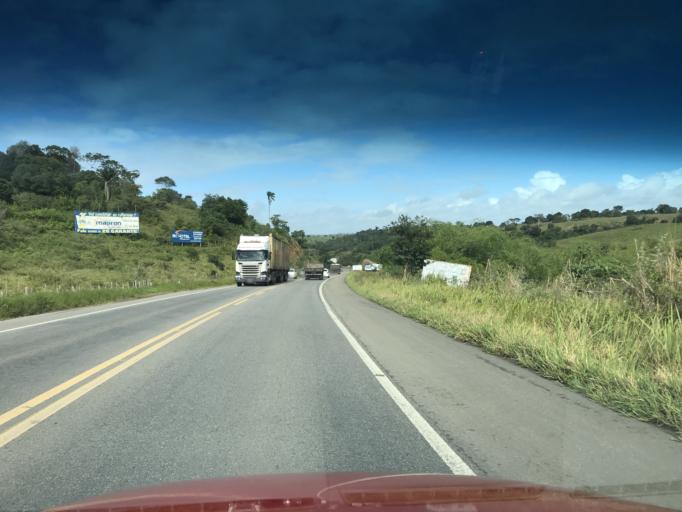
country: BR
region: Bahia
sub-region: Conceicao Do Almeida
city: Muritiba
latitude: -12.9214
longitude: -39.2476
